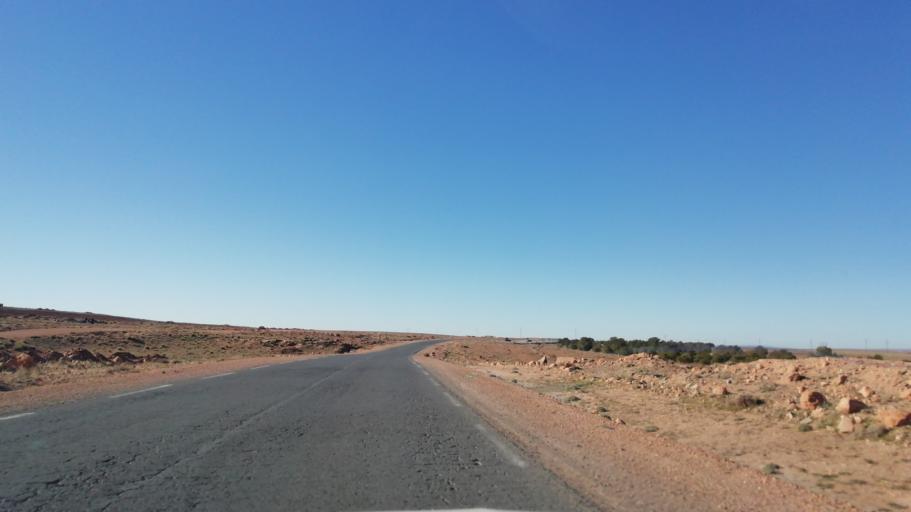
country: DZ
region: El Bayadh
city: El Bayadh
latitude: 33.6695
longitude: 0.9311
